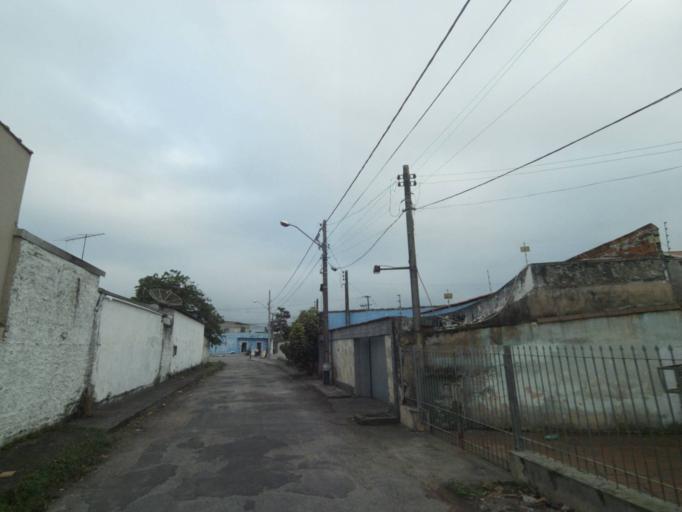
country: BR
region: Parana
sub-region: Paranagua
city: Paranagua
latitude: -25.5188
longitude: -48.5219
